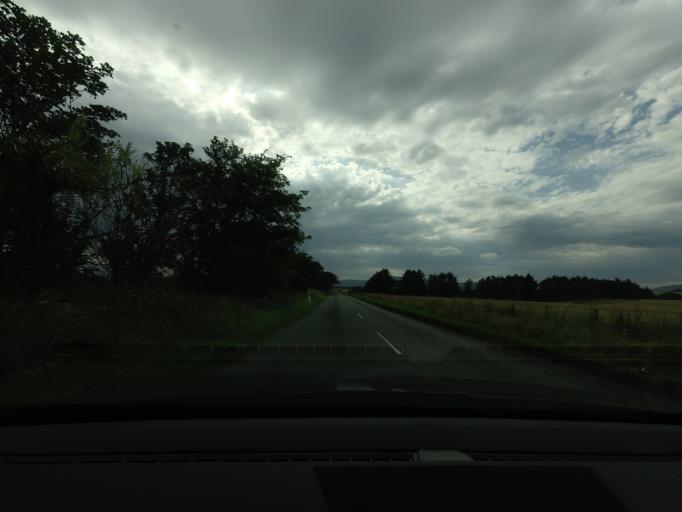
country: GB
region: Scotland
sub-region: Highland
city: Alness
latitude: 57.6912
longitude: -4.2199
